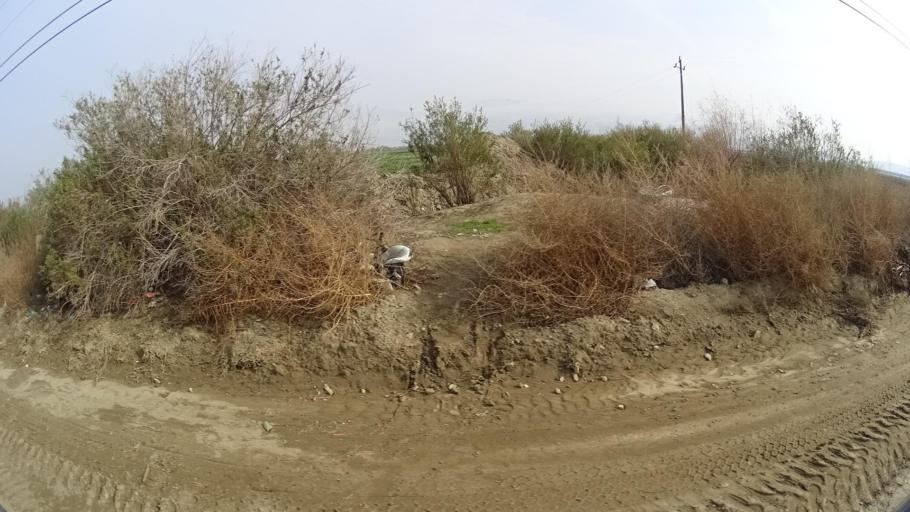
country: US
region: California
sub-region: Kern County
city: Arvin
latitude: 35.1765
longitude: -118.8510
